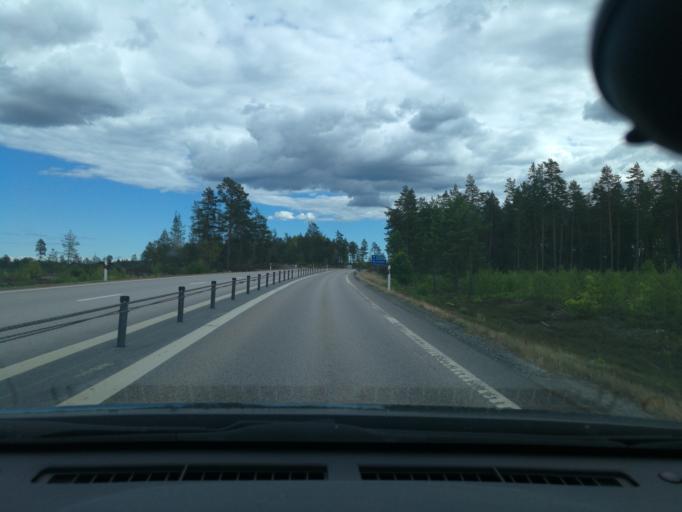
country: SE
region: Kalmar
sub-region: Vasterviks Kommun
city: Forserum
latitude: 58.0626
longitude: 16.5271
